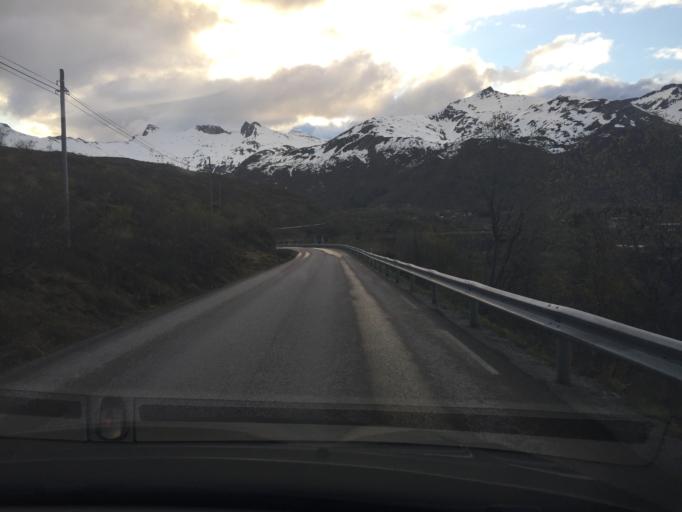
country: NO
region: Nordland
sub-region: Vagan
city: Svolvaer
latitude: 68.3171
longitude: 14.7122
